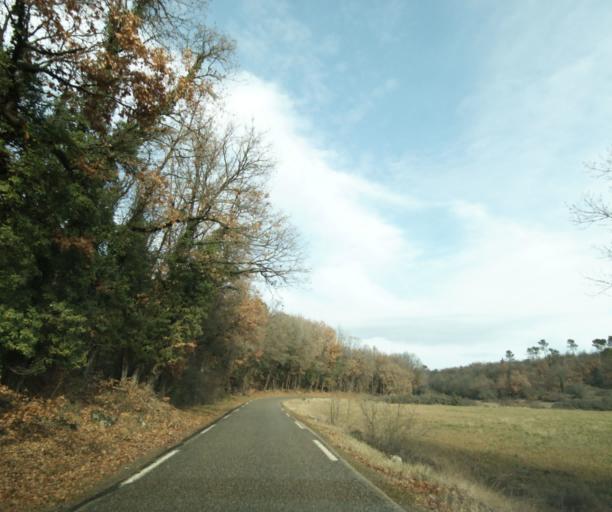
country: FR
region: Provence-Alpes-Cote d'Azur
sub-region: Departement du Var
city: Rougiers
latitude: 43.4139
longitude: 5.8688
